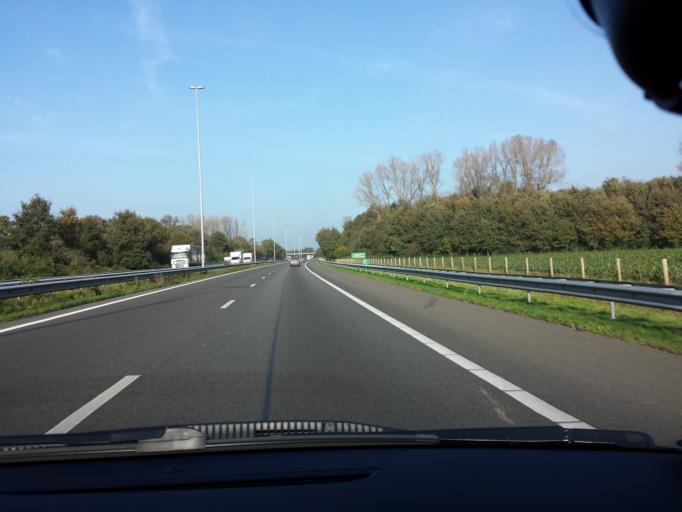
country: NL
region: North Brabant
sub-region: Gemeente Cuijk
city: Cuijk
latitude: 51.7107
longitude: 5.8725
